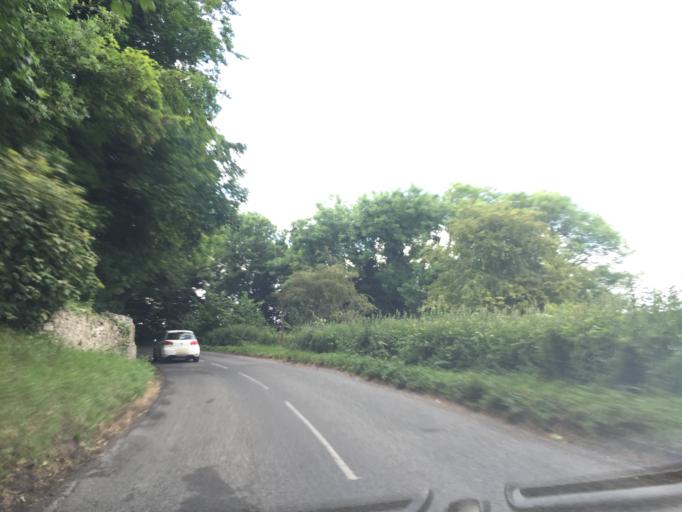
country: GB
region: England
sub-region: Dorset
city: Bovington Camp
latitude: 50.6578
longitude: -2.2746
